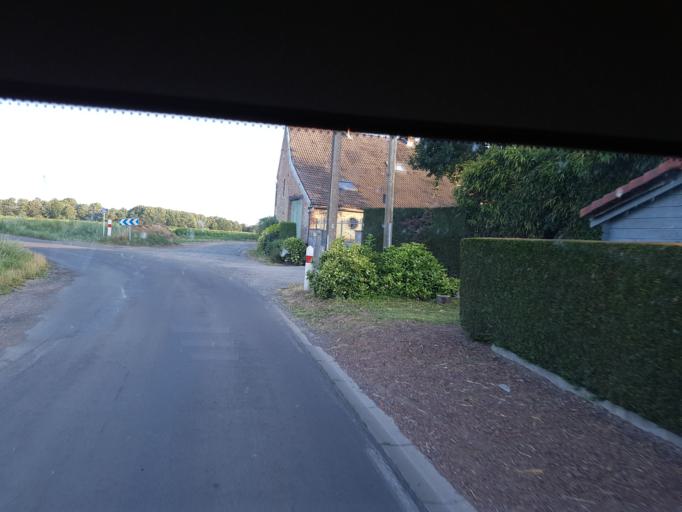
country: FR
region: Nord-Pas-de-Calais
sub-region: Departement du Nord
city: Hergnies
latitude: 50.4910
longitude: 3.5517
